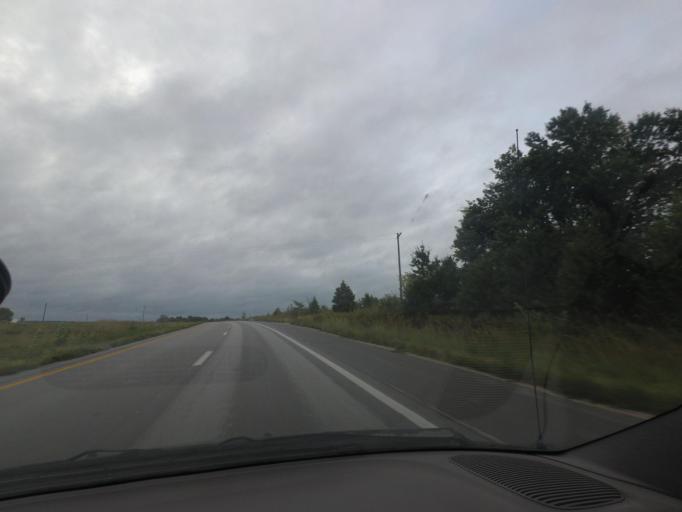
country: US
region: Missouri
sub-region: Shelby County
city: Shelbina
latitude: 39.6710
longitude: -91.9418
